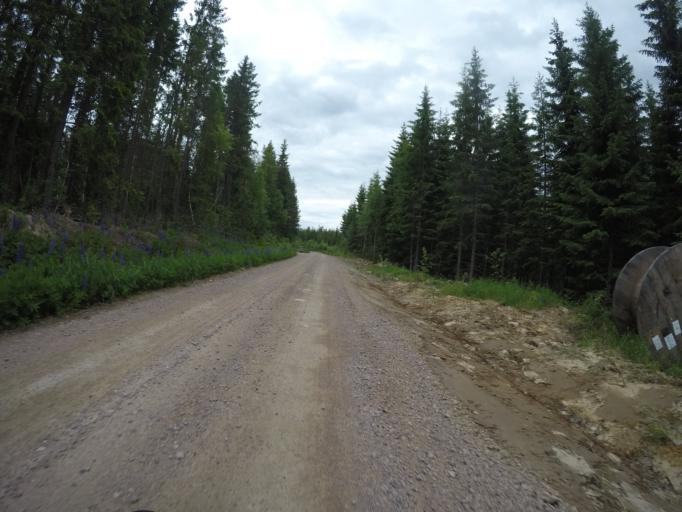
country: SE
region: Dalarna
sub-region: Ludvika Kommun
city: Abborrberget
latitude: 60.1054
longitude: 14.5207
